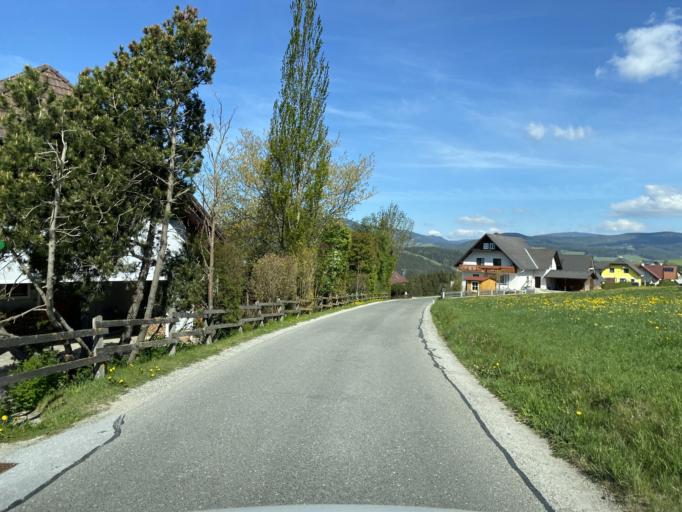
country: AT
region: Styria
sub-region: Politischer Bezirk Weiz
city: Birkfeld
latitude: 47.3604
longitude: 15.7048
